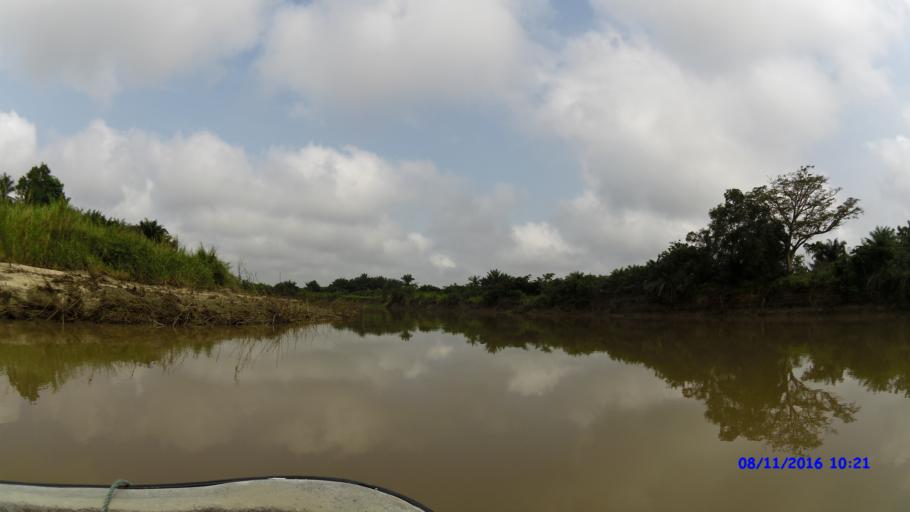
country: BJ
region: Mono
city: Come
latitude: 6.4060
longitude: 1.7760
